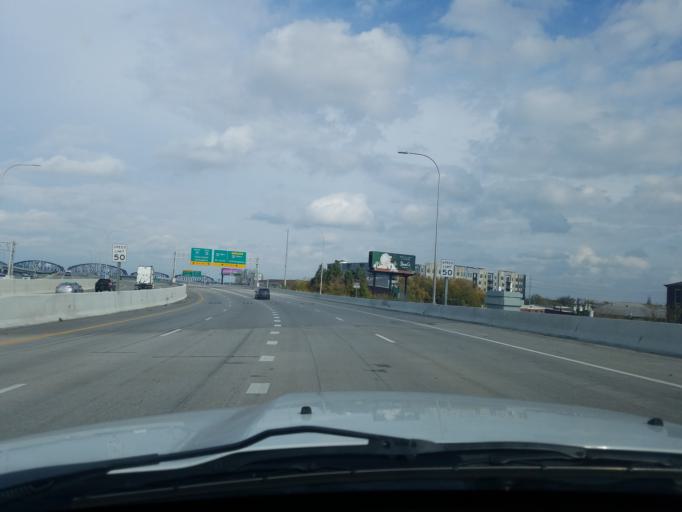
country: US
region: Kentucky
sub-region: Jefferson County
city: Louisville
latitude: 38.2527
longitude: -85.7429
